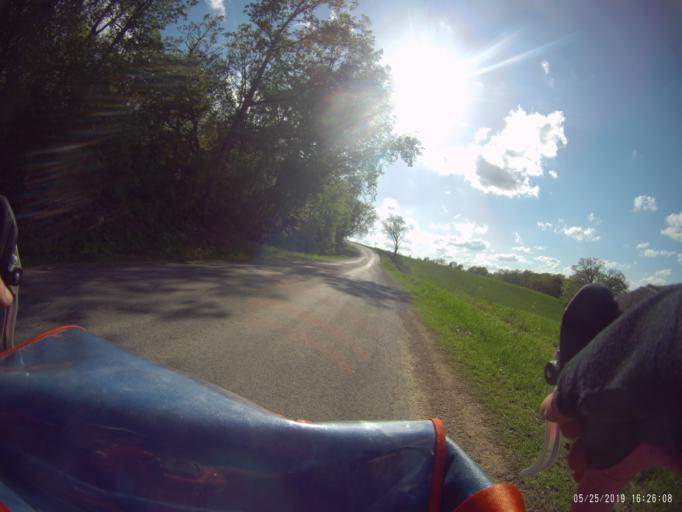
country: US
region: Wisconsin
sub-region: Dane County
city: Mount Horeb
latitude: 42.9509
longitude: -89.7047
